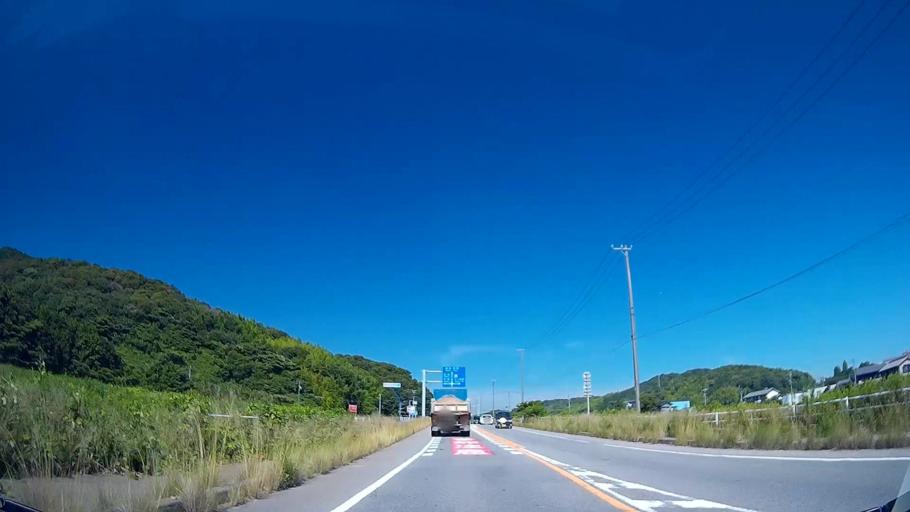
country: JP
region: Aichi
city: Gamagori
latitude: 34.8305
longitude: 137.1792
